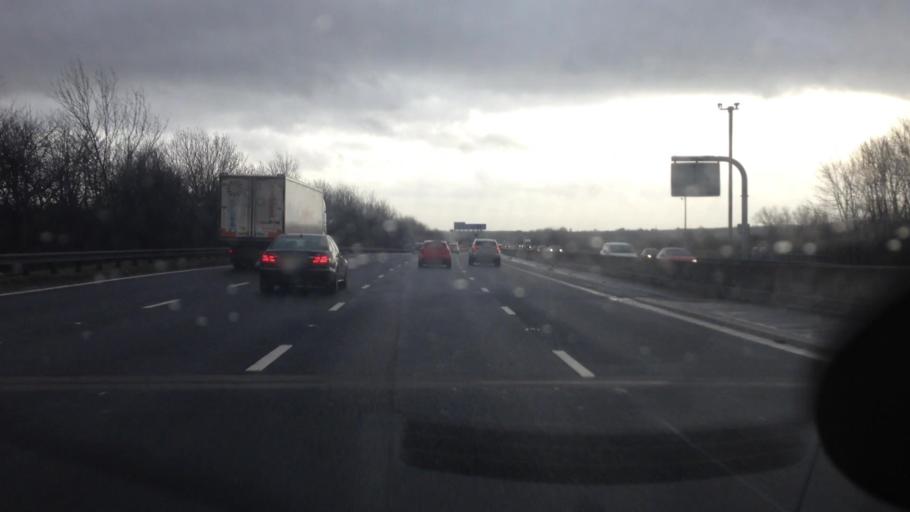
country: GB
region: England
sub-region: City and Borough of Wakefield
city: Horbury
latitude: 53.6656
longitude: -1.5387
